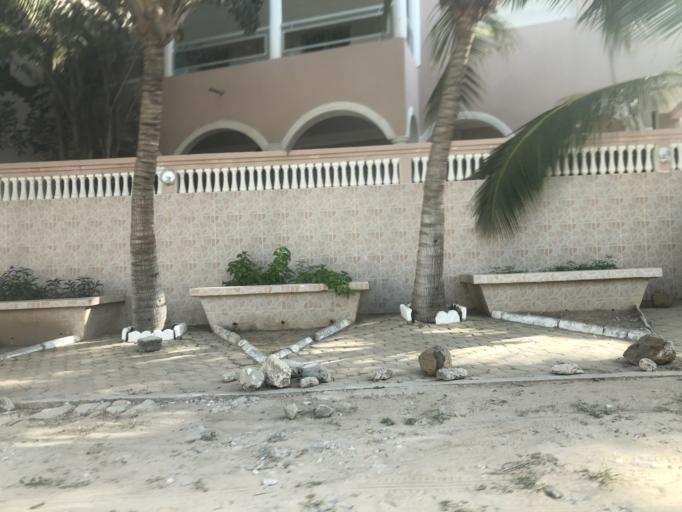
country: SN
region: Dakar
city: Mermoz Boabab
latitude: 14.7411
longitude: -17.5129
